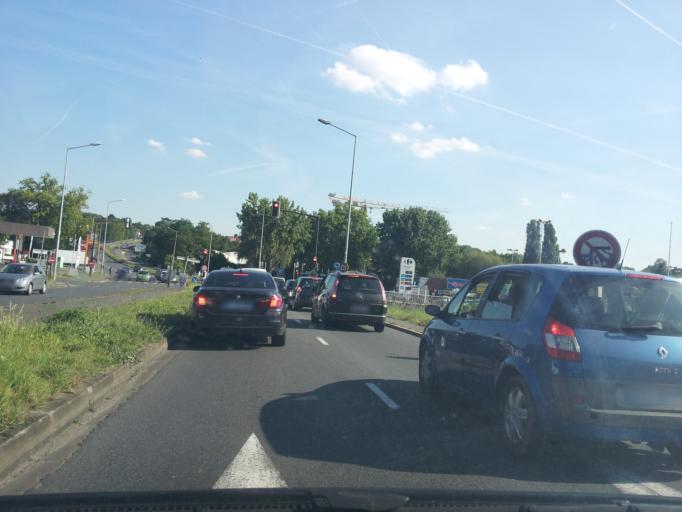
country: FR
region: Ile-de-France
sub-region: Departement de l'Essonne
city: Villemoisson-sur-Orge
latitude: 48.6692
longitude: 2.3380
